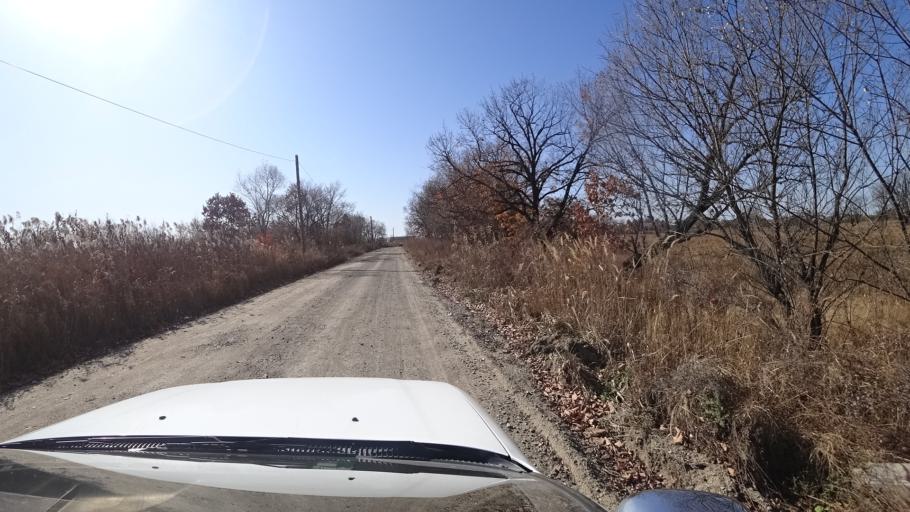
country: RU
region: Primorskiy
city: Dal'nerechensk
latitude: 45.9254
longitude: 133.7838
